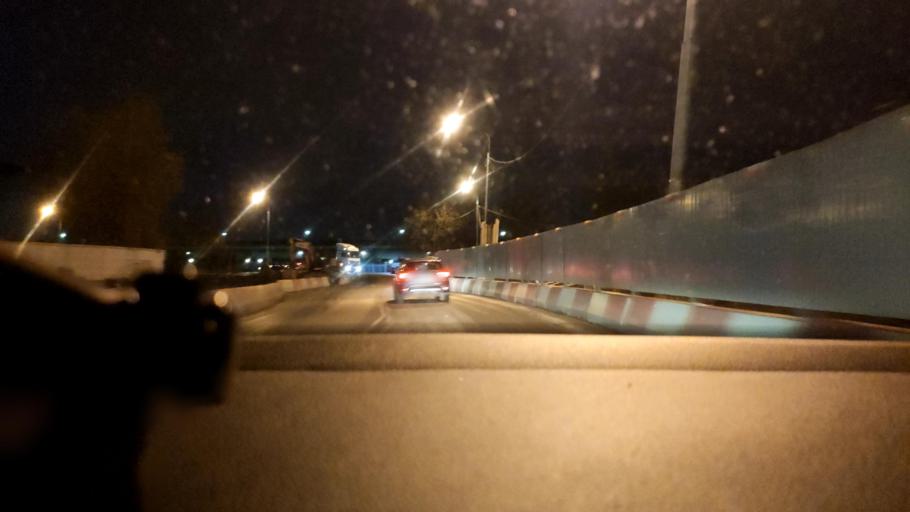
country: RU
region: Moskovskaya
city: Kur'yanovo
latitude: 55.6467
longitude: 37.6913
